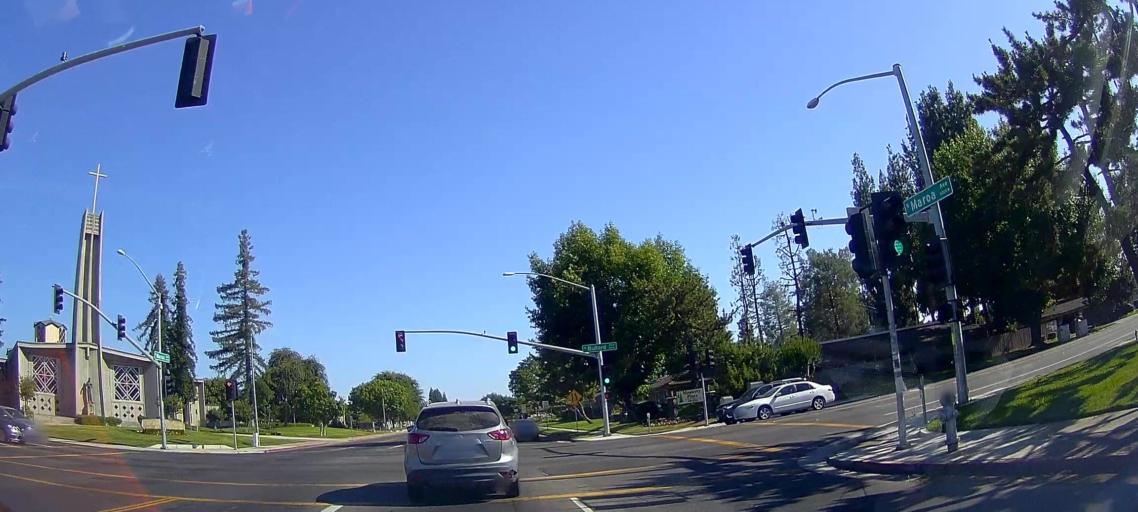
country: US
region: California
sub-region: Fresno County
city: Fresno
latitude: 36.8231
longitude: -119.7994
